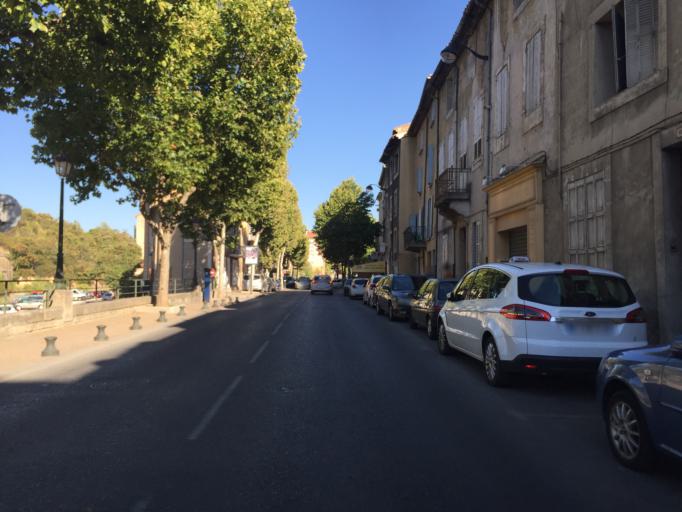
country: FR
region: Provence-Alpes-Cote d'Azur
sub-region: Departement du Vaucluse
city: Apt
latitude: 43.8771
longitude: 5.3976
